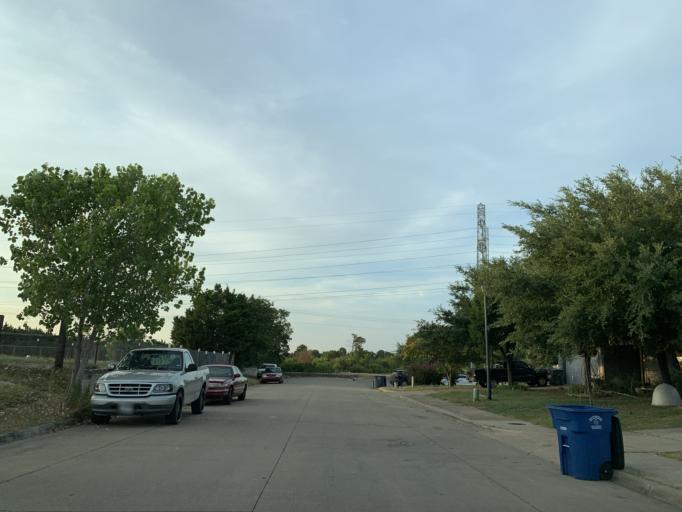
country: US
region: Texas
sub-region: Dallas County
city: Cockrell Hill
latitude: 32.7018
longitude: -96.8850
